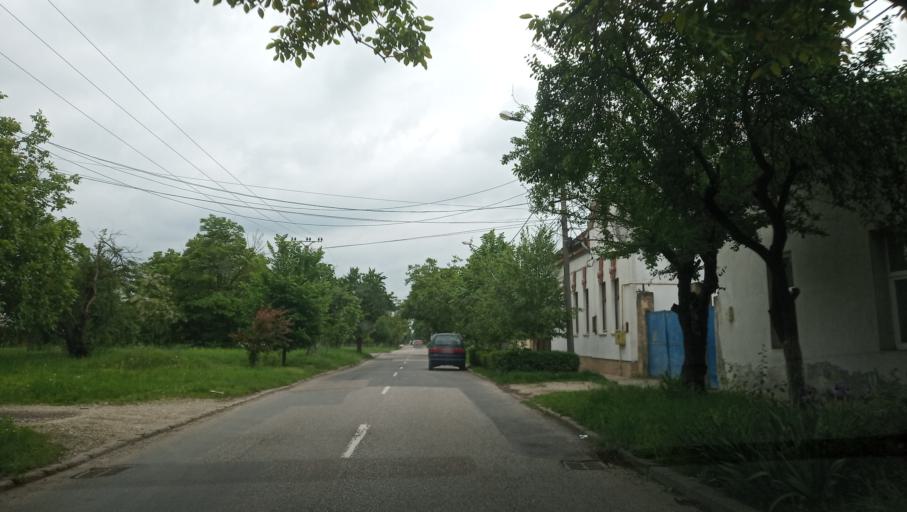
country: RO
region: Timis
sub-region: Comuna Ghiroda
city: Ghiroda
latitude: 45.7551
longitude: 21.2636
